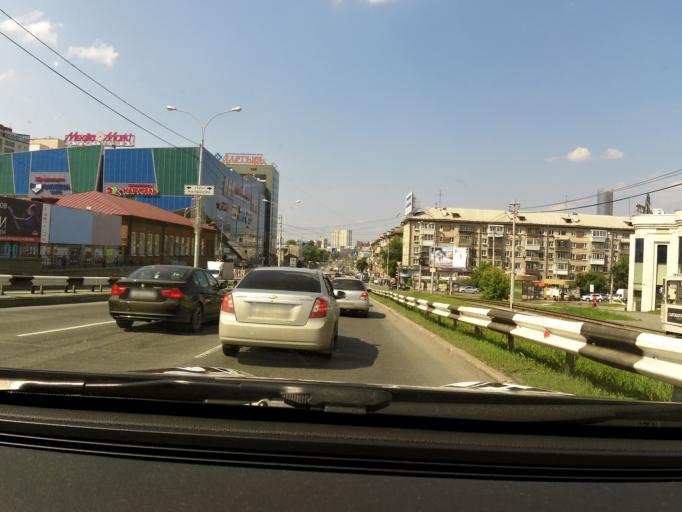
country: RU
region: Sverdlovsk
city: Yekaterinburg
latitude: 56.8313
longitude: 60.5841
